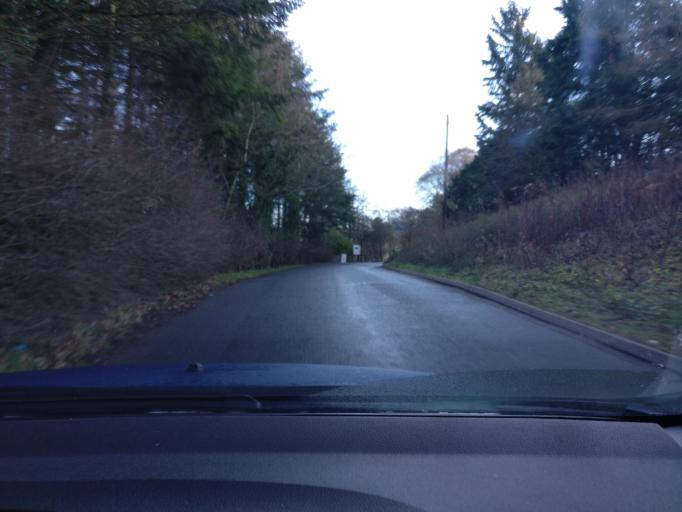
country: GB
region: Scotland
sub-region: The Scottish Borders
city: Hawick
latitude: 55.4429
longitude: -2.7390
